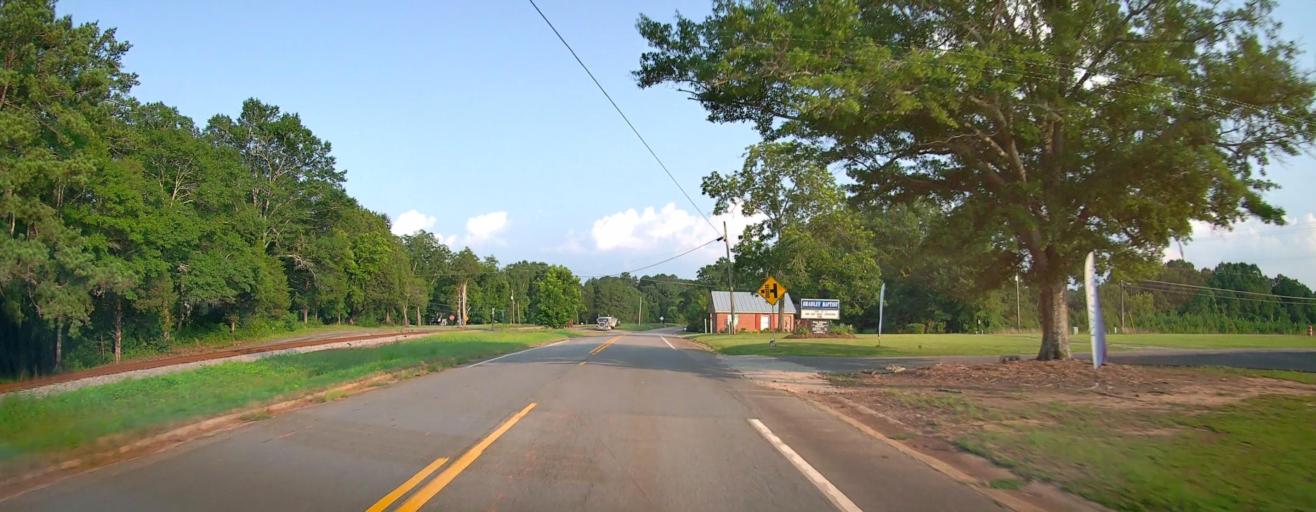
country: US
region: Georgia
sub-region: Jones County
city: Gray
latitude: 33.0550
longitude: -83.5596
